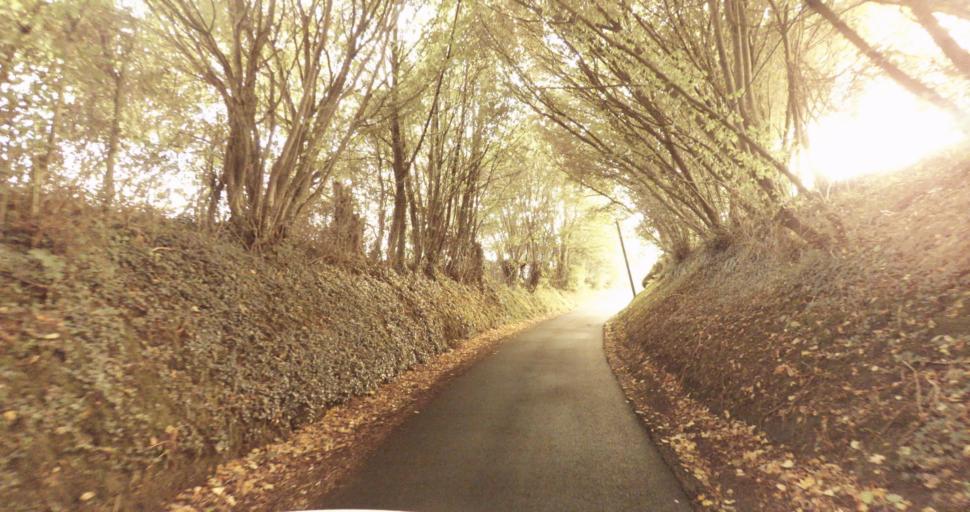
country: FR
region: Lower Normandy
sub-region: Departement de l'Orne
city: Vimoutiers
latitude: 48.9316
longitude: 0.2095
